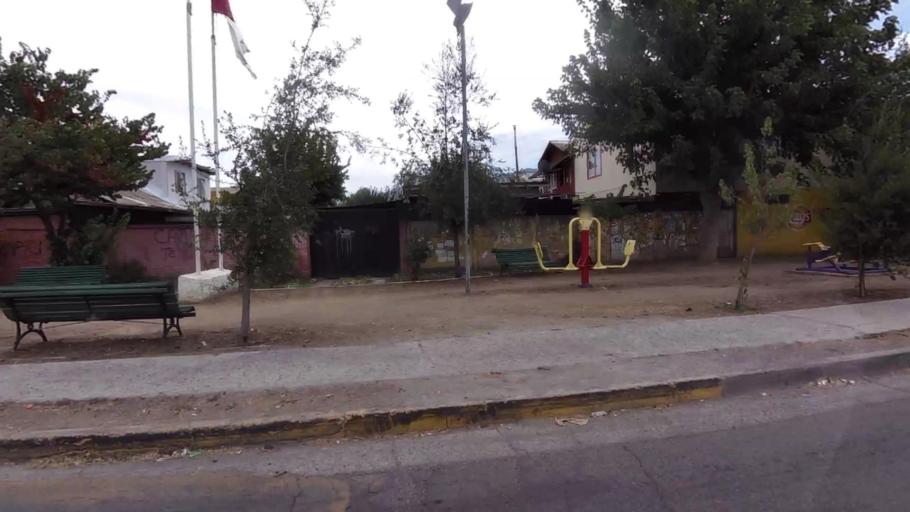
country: CL
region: O'Higgins
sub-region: Provincia de Cachapoal
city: Graneros
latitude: -34.0671
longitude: -70.7231
